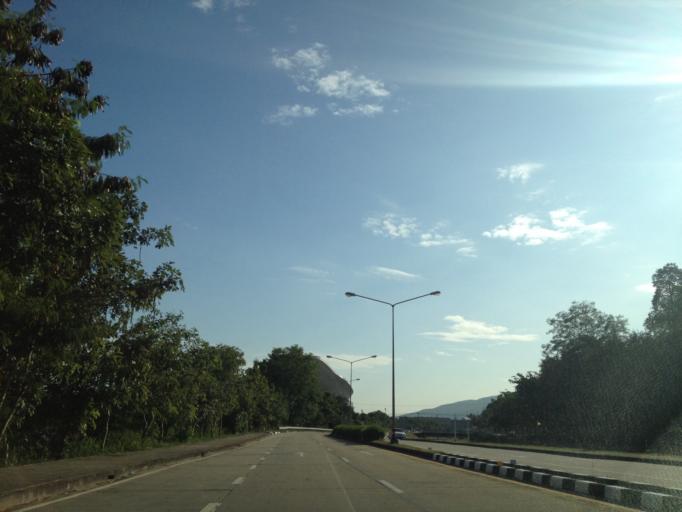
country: TH
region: Chiang Mai
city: Chiang Mai
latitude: 18.8540
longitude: 98.9623
